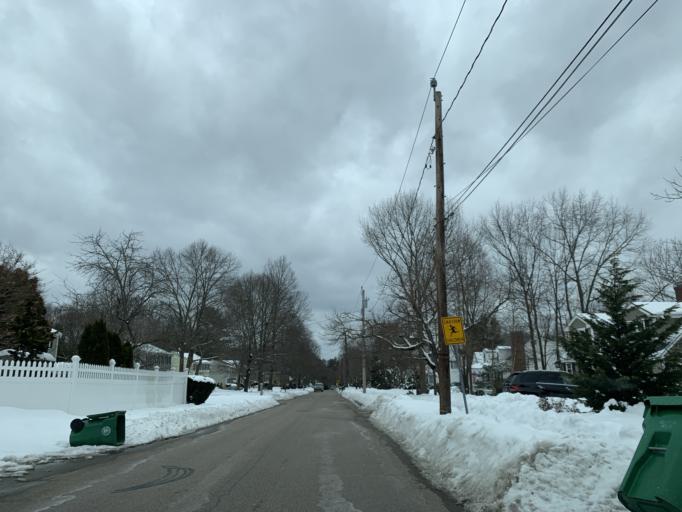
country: US
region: Massachusetts
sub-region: Norfolk County
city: Dedham
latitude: 42.2122
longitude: -71.1706
